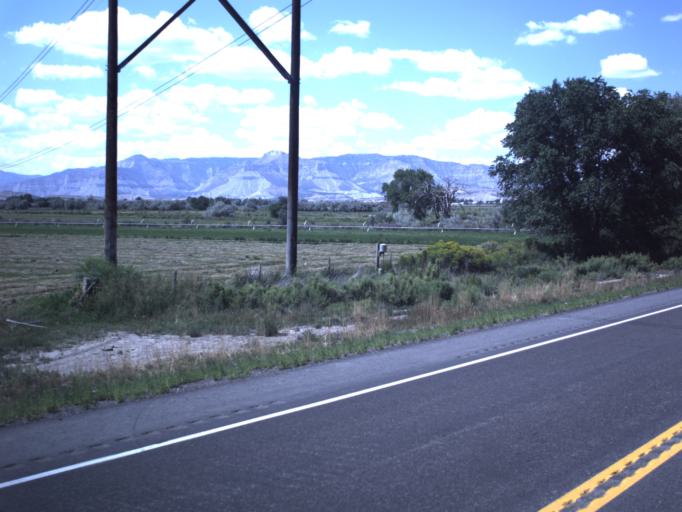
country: US
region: Utah
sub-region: Emery County
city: Huntington
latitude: 39.2991
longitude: -110.9645
